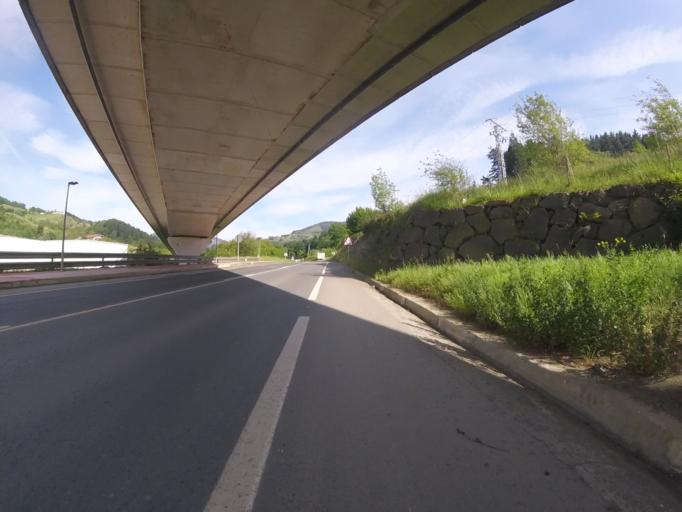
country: ES
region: Basque Country
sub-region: Provincia de Guipuzcoa
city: Gabiria
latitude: 43.0739
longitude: -2.2890
